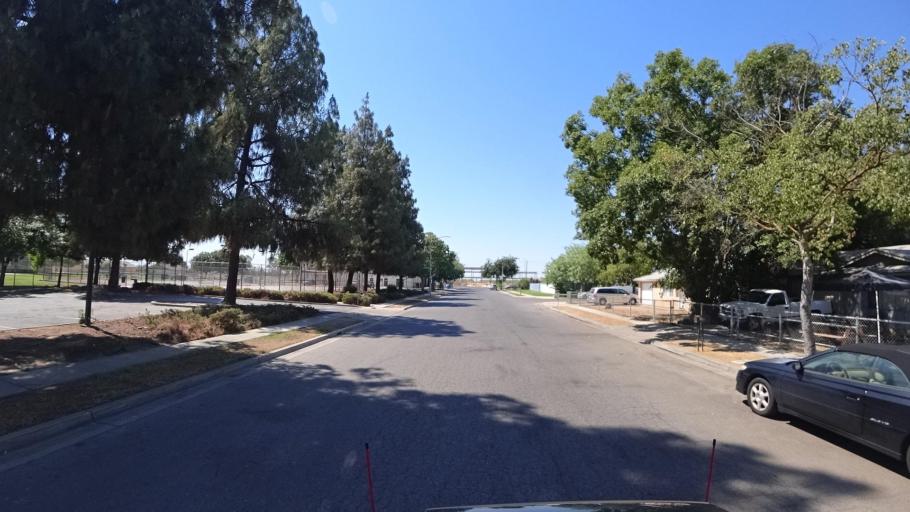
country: US
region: California
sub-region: Fresno County
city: Fresno
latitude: 36.7155
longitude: -119.8044
